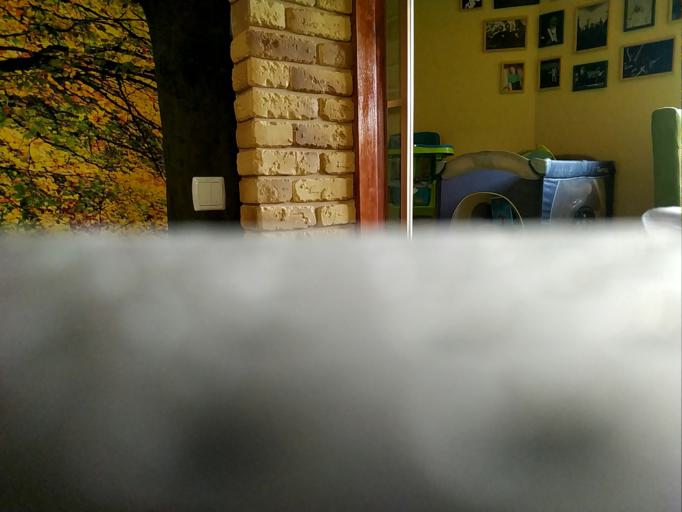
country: RU
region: Kaluga
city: Seredeyskiy
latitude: 53.9824
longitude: 35.3241
